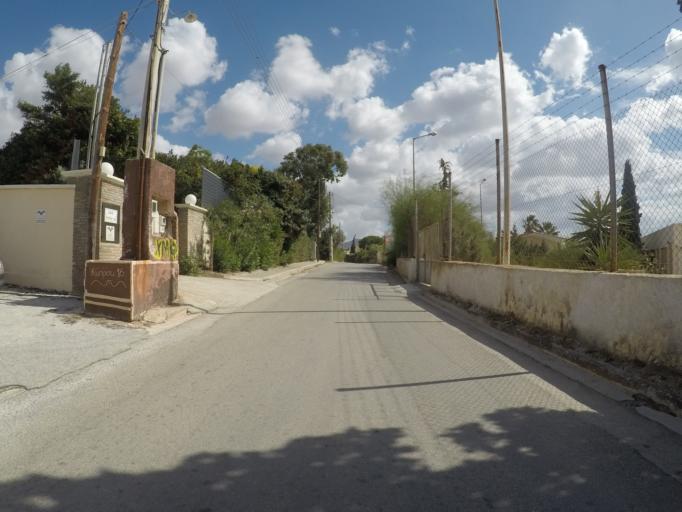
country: GR
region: Attica
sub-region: Nomarchia Anatolikis Attikis
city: Agios Dimitrios Kropias
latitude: 37.7983
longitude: 23.8726
